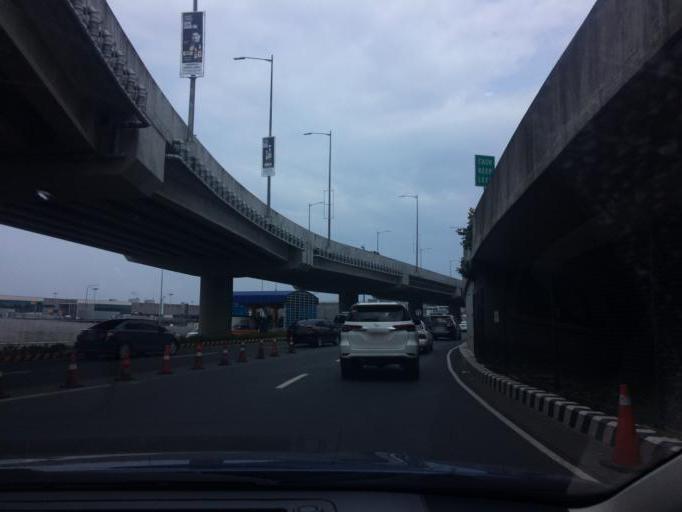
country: PH
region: Metro Manila
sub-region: Makati City
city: Makati City
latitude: 14.5173
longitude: 121.0191
